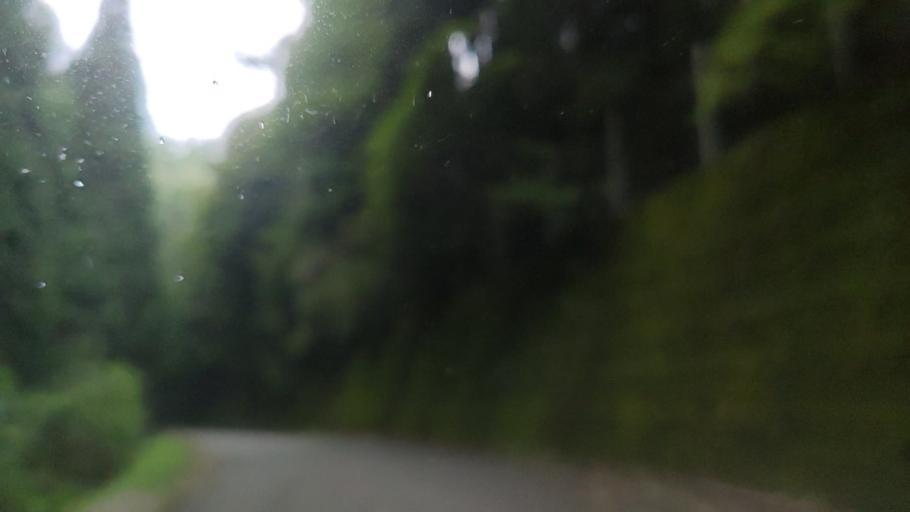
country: JP
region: Wakayama
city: Hashimoto
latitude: 34.2820
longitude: 135.6283
